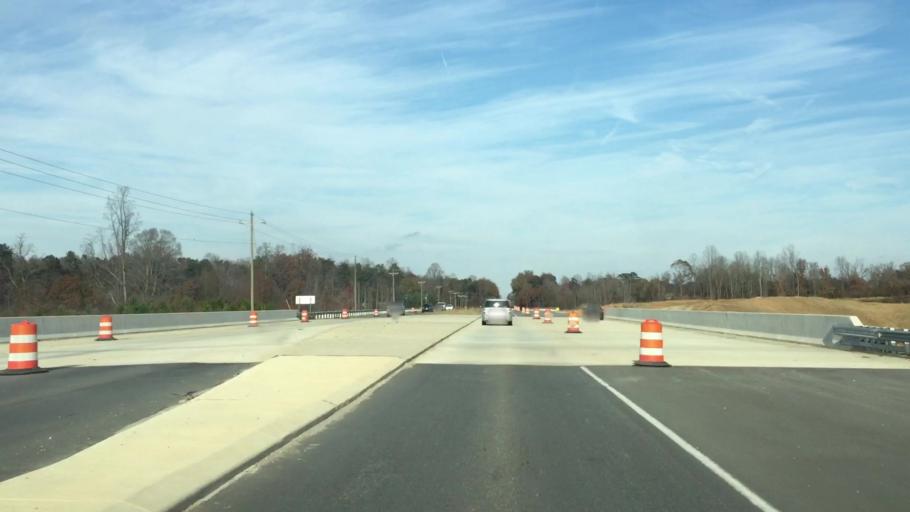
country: US
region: North Carolina
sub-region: Forsyth County
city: Walkertown
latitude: 36.1456
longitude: -80.1568
